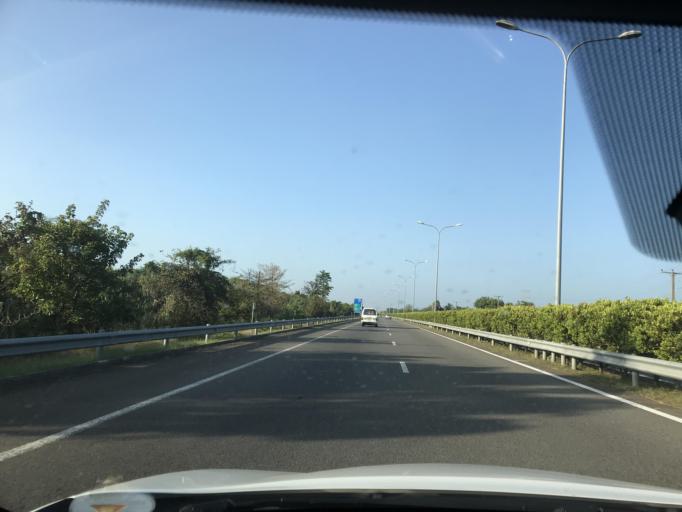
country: LK
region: Western
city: Ja Ela
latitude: 7.0682
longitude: 79.8786
